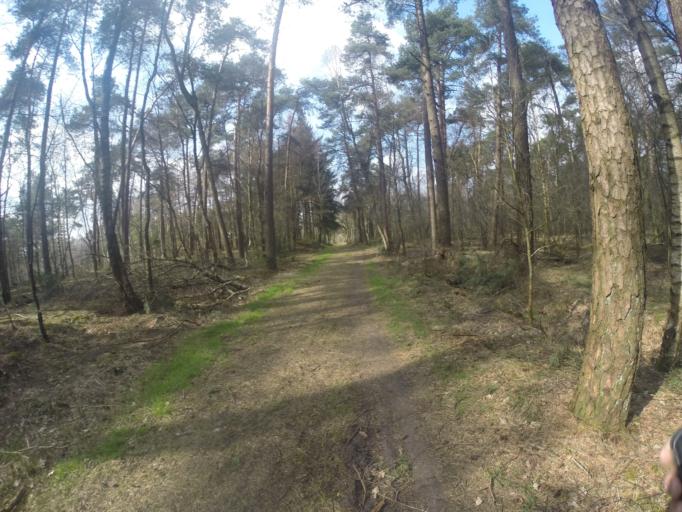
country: NL
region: Gelderland
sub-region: Gemeente Lochem
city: Almen
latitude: 52.1463
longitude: 6.3245
